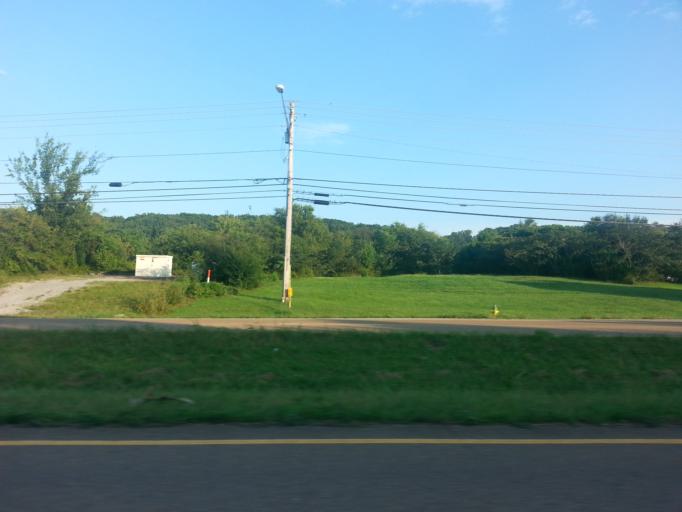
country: US
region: Tennessee
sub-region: McMinn County
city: Athens
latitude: 35.4889
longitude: -84.5825
